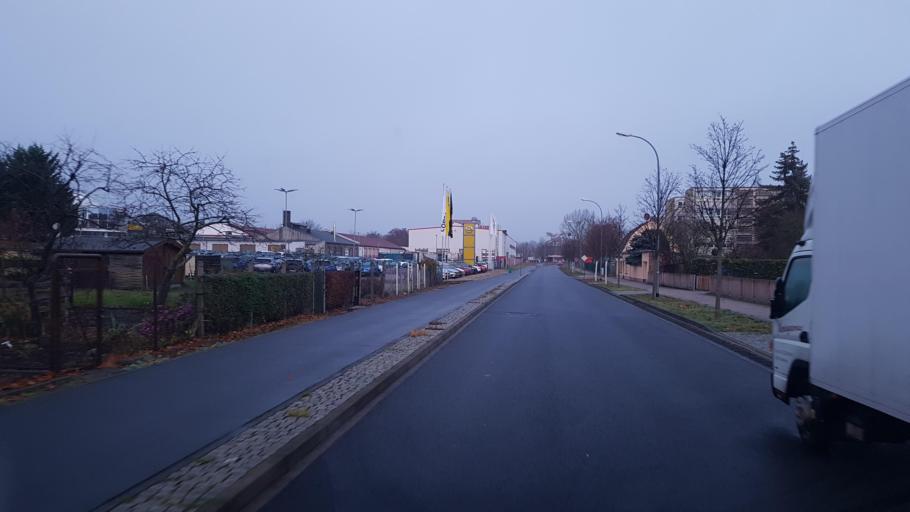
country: DE
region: Brandenburg
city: Luckenwalde
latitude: 52.0807
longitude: 13.1569
